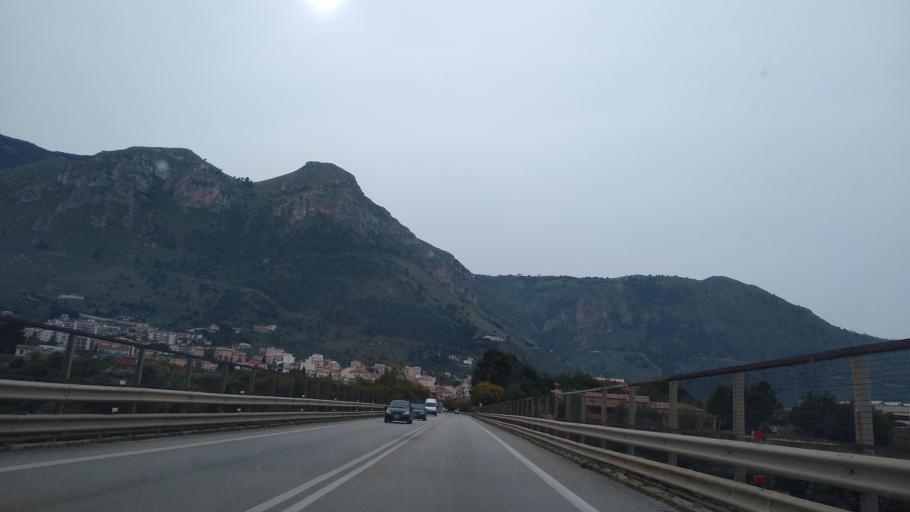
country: IT
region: Sicily
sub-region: Trapani
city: Castellammare del Golfo
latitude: 38.0159
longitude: 12.8973
